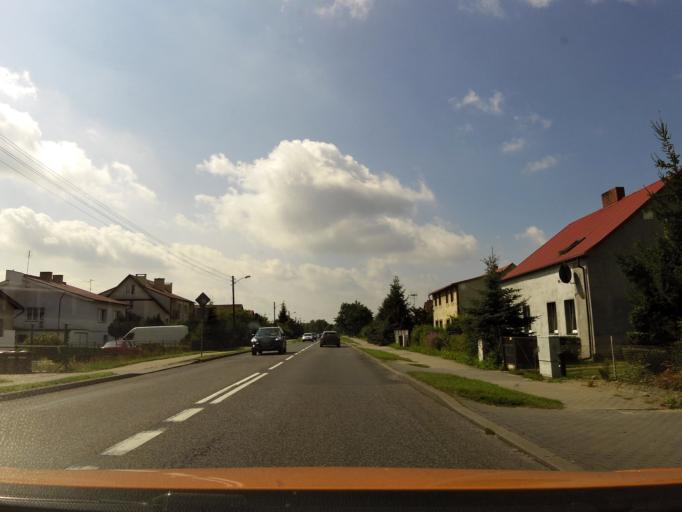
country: PL
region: West Pomeranian Voivodeship
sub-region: Powiat gryficki
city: Ploty
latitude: 53.7982
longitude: 15.2590
